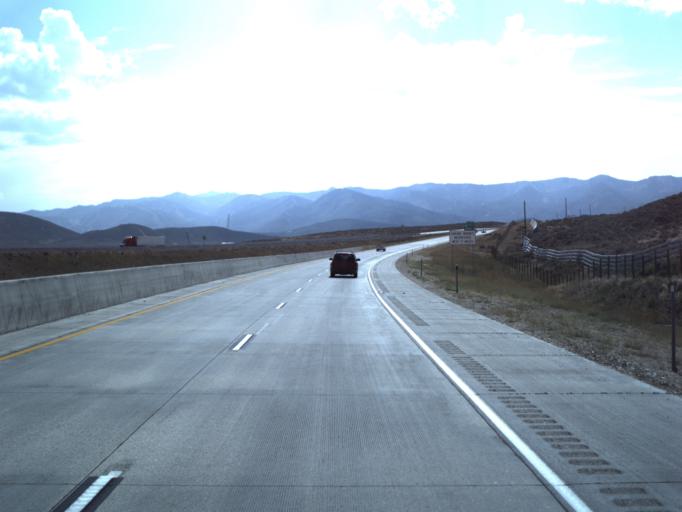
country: US
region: Utah
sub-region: Summit County
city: Snyderville
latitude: 40.7441
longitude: -111.4748
